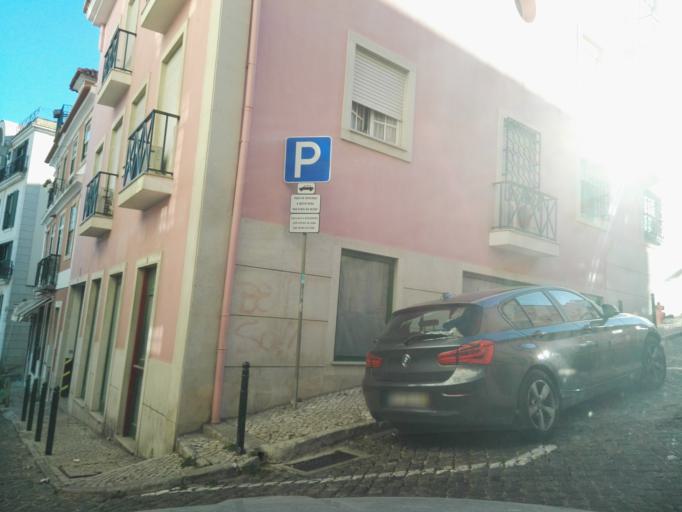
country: PT
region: Setubal
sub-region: Almada
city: Cacilhas
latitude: 38.7058
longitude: -9.1618
